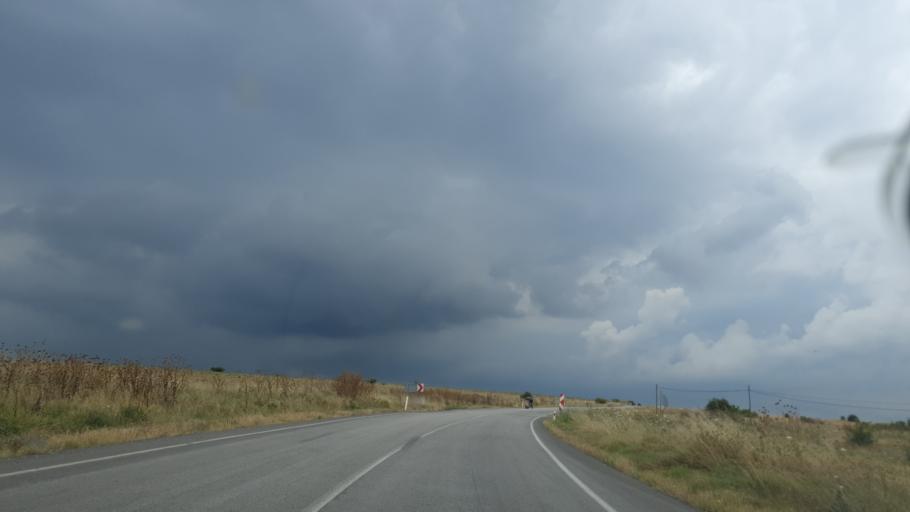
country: TR
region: Tekirdag
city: Hayrabolu
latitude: 41.2184
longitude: 27.0604
